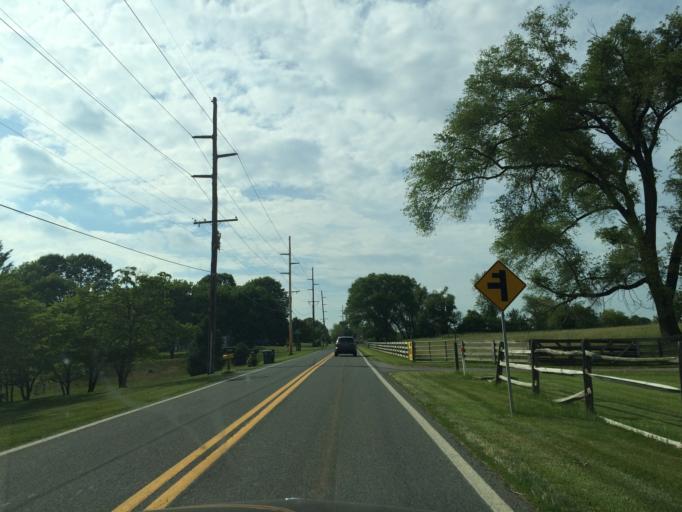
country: US
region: Maryland
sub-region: Carroll County
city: Eldersburg
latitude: 39.4730
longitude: -76.9101
